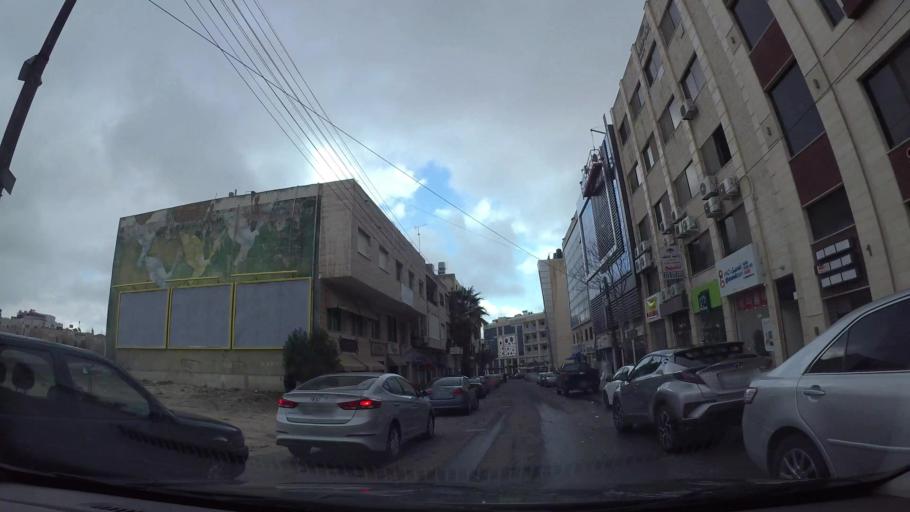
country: JO
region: Amman
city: Wadi as Sir
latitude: 31.9512
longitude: 35.8723
